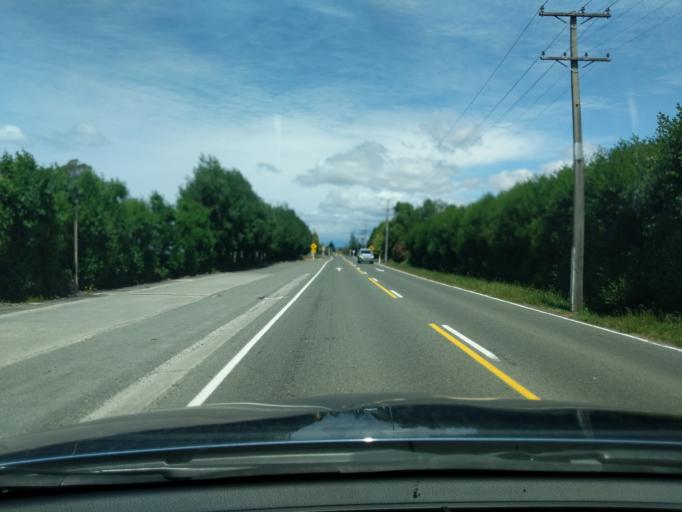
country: NZ
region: Tasman
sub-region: Tasman District
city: Motueka
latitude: -41.0887
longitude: 172.9968
